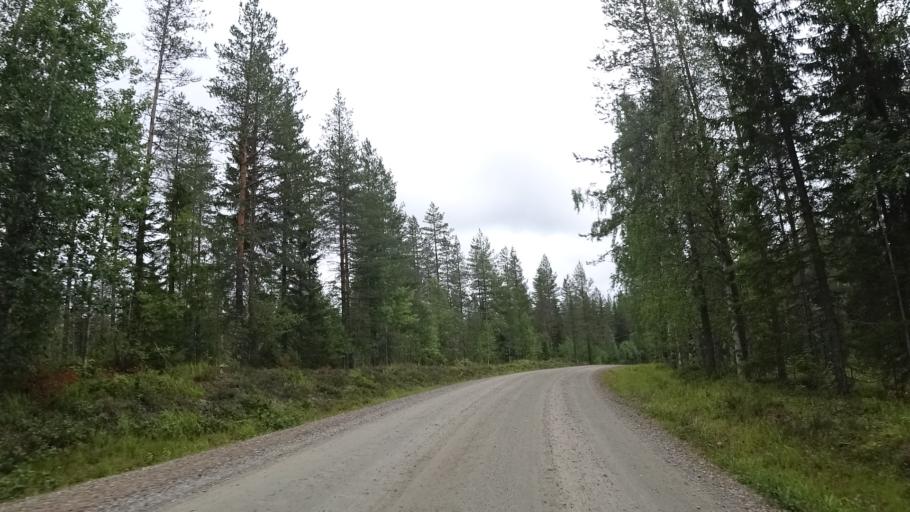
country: FI
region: North Karelia
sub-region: Joensuu
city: Ilomantsi
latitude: 63.0364
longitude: 31.2063
